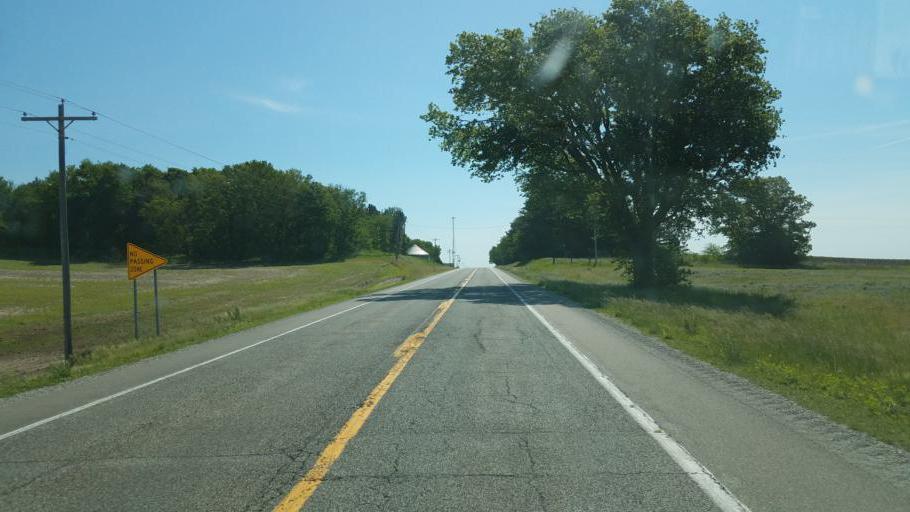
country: US
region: Illinois
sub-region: Mason County
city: Manito
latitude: 40.3035
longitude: -89.7829
